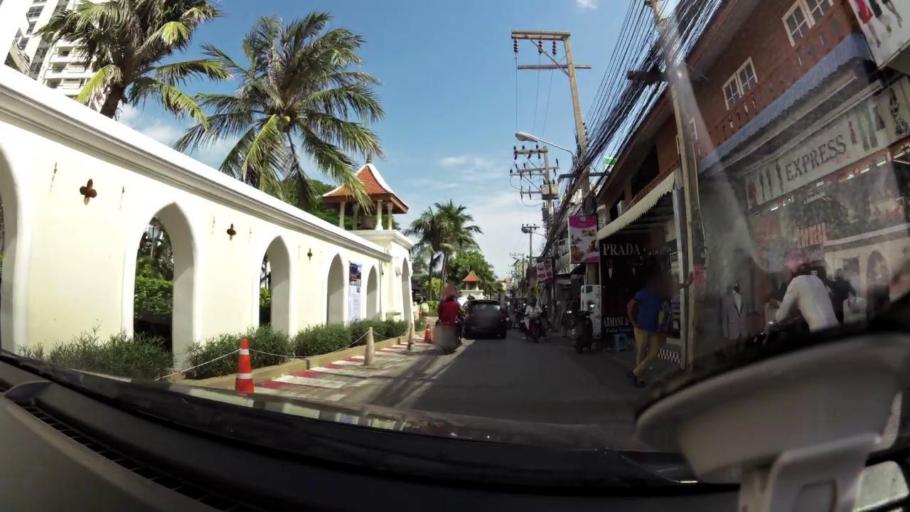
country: TH
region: Prachuap Khiri Khan
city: Hua Hin
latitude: 12.5711
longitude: 99.9601
